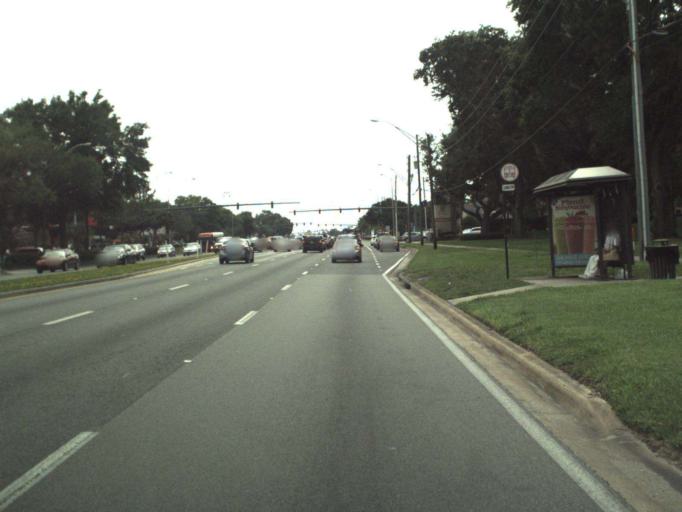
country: US
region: Florida
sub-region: Seminole County
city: Altamonte Springs
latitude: 28.6640
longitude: -81.3694
